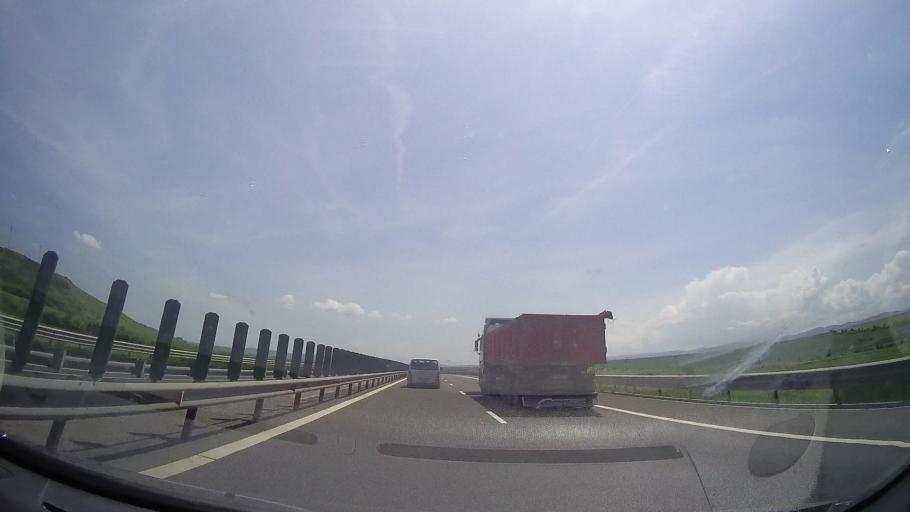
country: RO
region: Alba
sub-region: Comuna Garbova
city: Garbova
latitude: 45.9053
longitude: 23.7495
